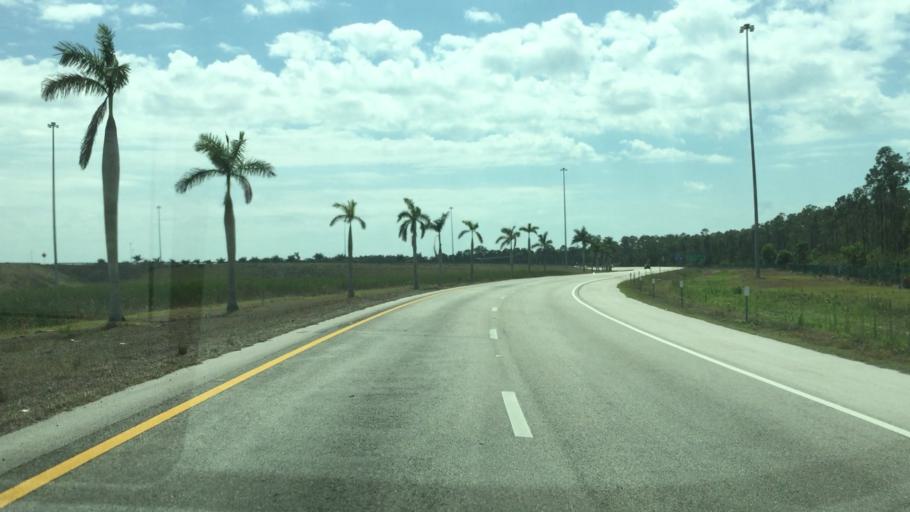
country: US
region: Florida
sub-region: Lee County
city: Three Oaks
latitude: 26.4977
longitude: -81.7952
